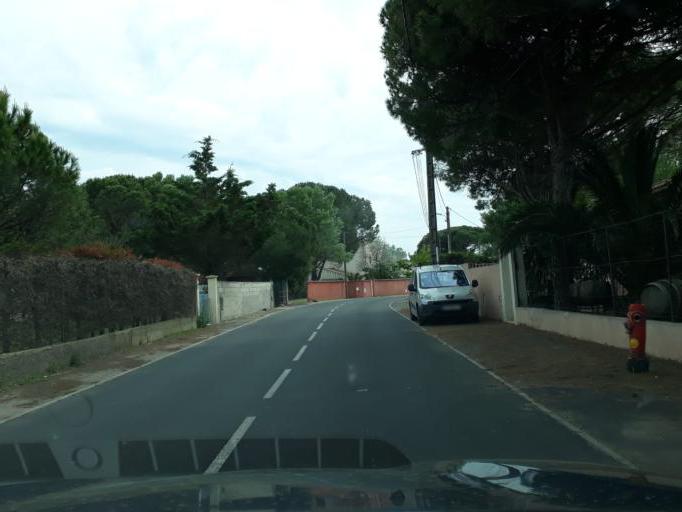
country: FR
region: Languedoc-Roussillon
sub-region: Departement de l'Herault
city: Agde
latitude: 43.2810
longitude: 3.4686
